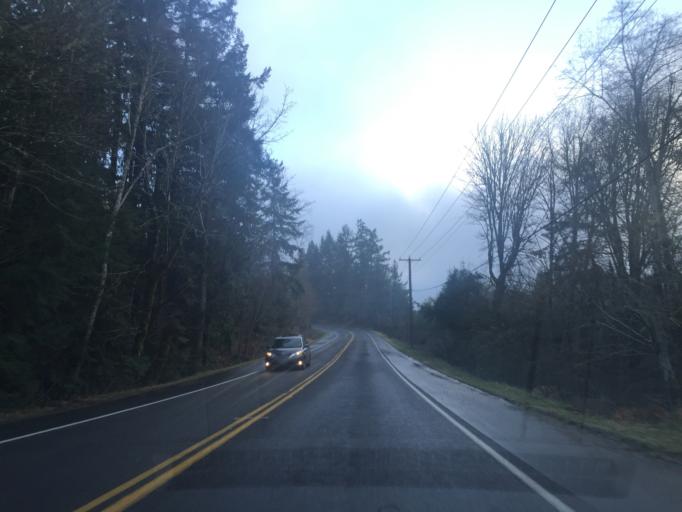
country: US
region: Washington
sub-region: Thurston County
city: Olympia
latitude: 47.1201
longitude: -122.8844
